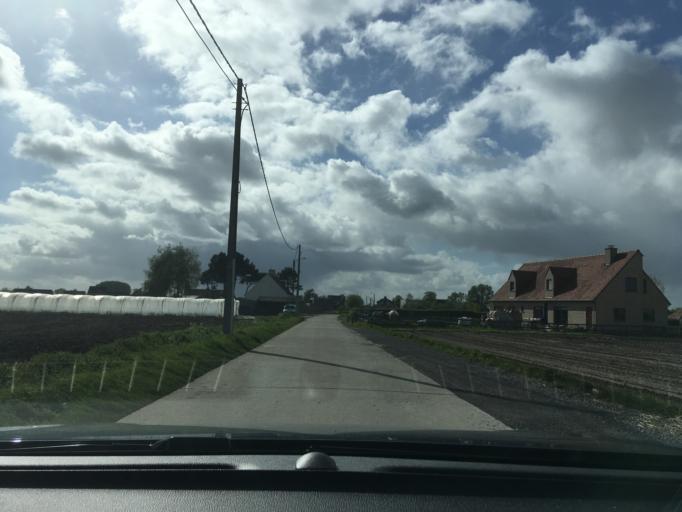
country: BE
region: Flanders
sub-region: Provincie West-Vlaanderen
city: Hooglede
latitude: 50.9998
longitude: 3.0568
